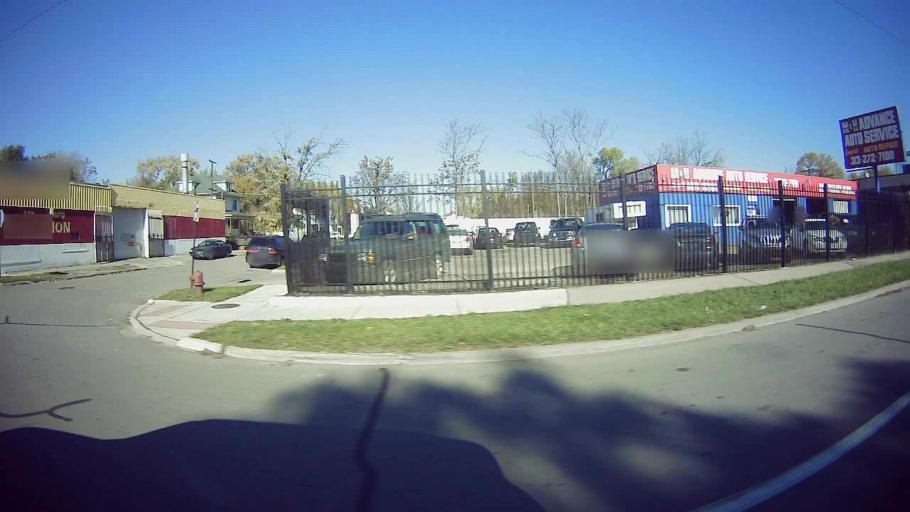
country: US
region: Michigan
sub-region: Wayne County
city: Dearborn
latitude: 42.3725
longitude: -83.2106
